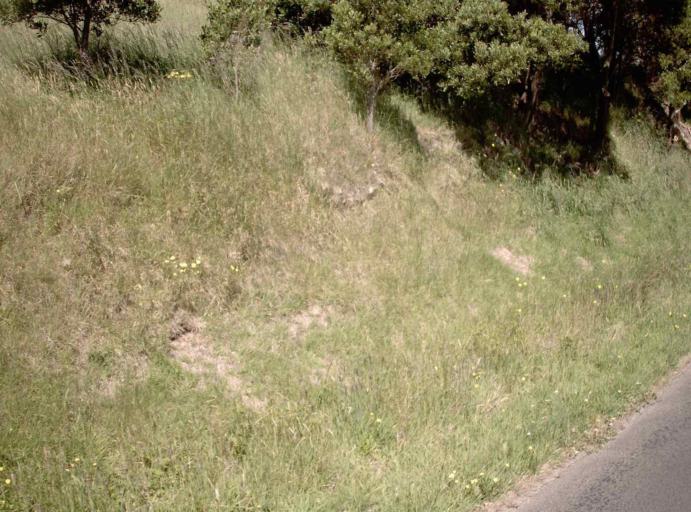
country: AU
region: Victoria
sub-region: Latrobe
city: Morwell
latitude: -38.6487
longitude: 146.2896
